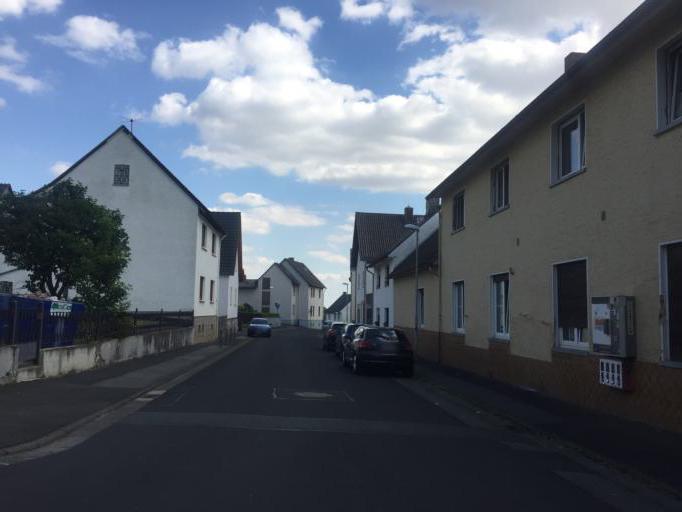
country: DE
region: Hesse
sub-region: Regierungsbezirk Giessen
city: Heuchelheim
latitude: 50.6207
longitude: 8.6106
